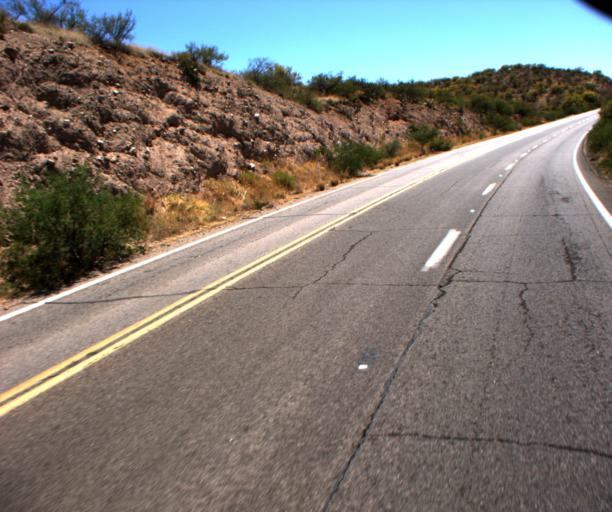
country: US
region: Arizona
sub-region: Pinal County
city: Mammoth
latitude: 32.6716
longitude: -110.6653
